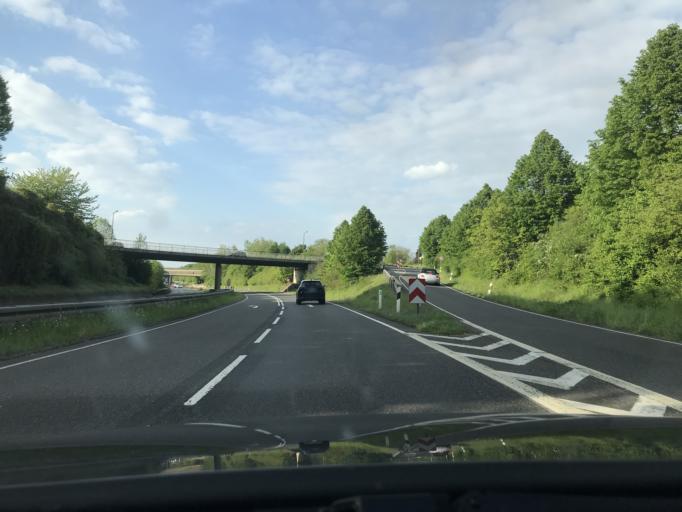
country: DE
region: North Rhine-Westphalia
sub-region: Regierungsbezirk Koln
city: Erftstadt
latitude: 50.8088
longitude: 6.8061
